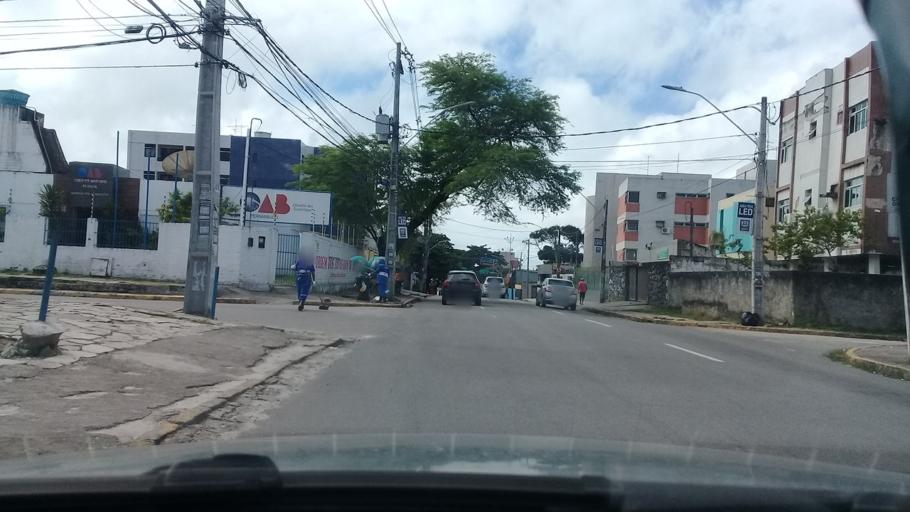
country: BR
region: Pernambuco
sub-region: Jaboatao Dos Guararapes
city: Jaboatao
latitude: -8.1653
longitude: -34.9175
